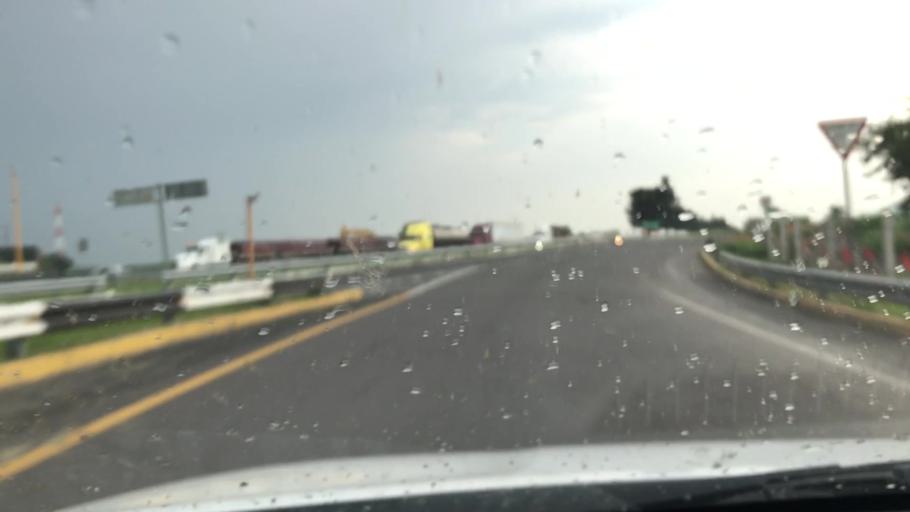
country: MX
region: Michoacan
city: Vistahermosa de Negrete
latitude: 20.2700
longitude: -102.4407
